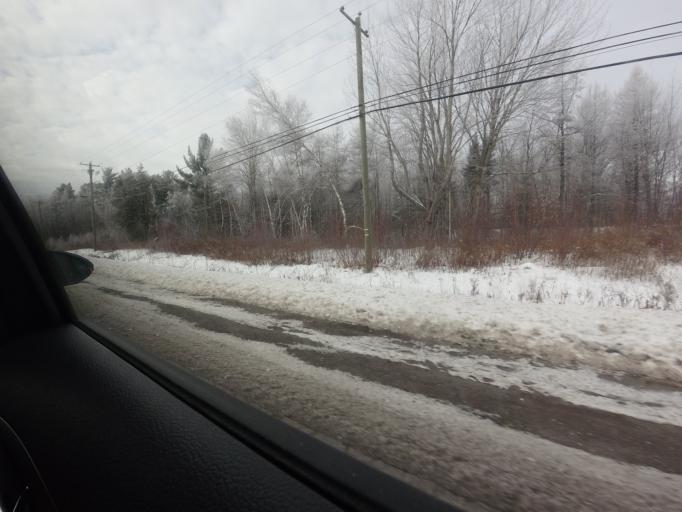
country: CA
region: New Brunswick
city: Oromocto
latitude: 45.8588
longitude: -66.4525
